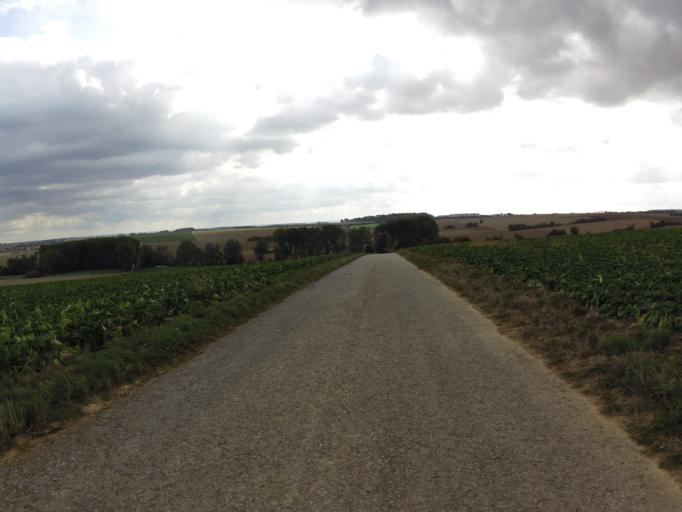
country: DE
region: Bavaria
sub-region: Regierungsbezirk Unterfranken
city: Reichenberg
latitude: 49.7125
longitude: 9.9481
